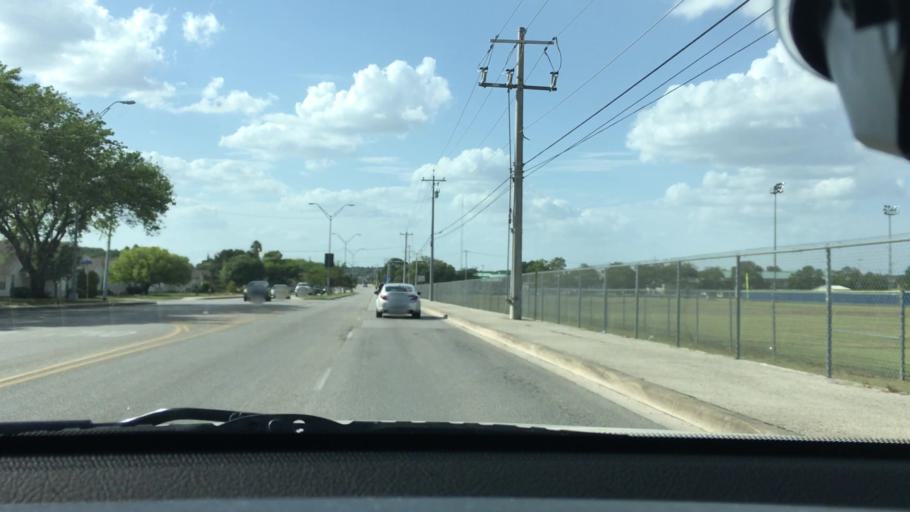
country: US
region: Texas
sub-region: Guadalupe County
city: Schertz
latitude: 29.5612
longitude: -98.2676
